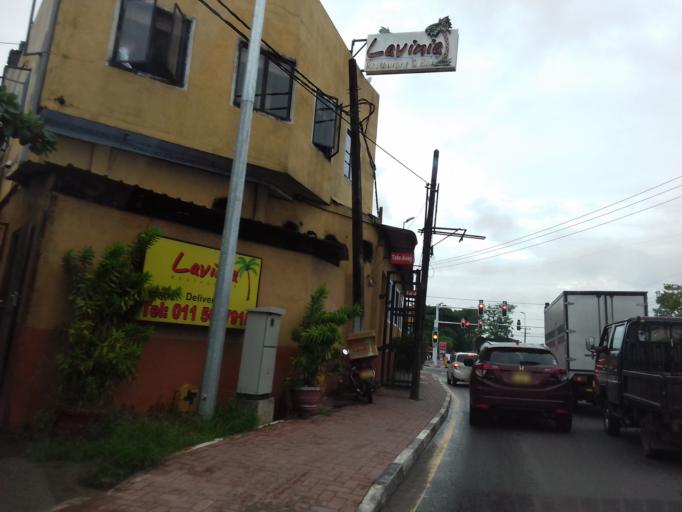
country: LK
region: Western
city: Battaramulla South
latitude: 6.8945
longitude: 79.9240
